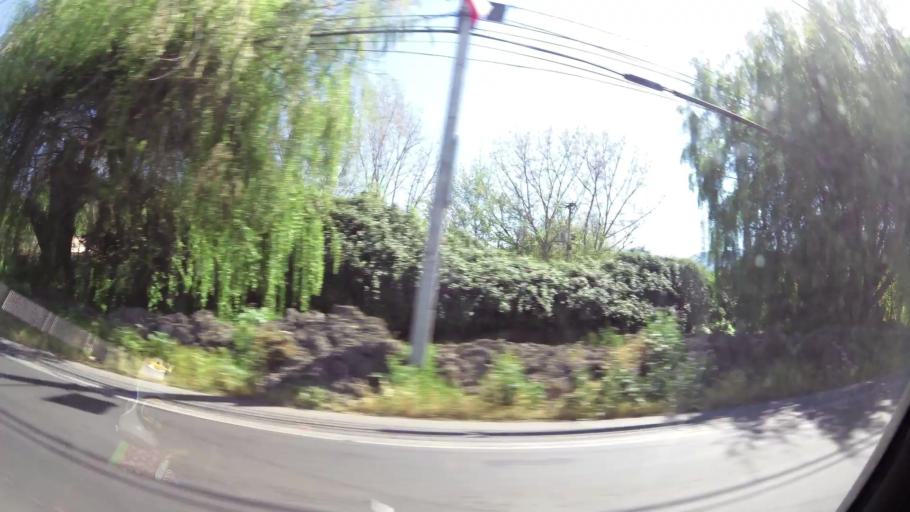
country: CL
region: Santiago Metropolitan
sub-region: Provincia de Talagante
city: Penaflor
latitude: -33.6236
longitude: -70.9089
